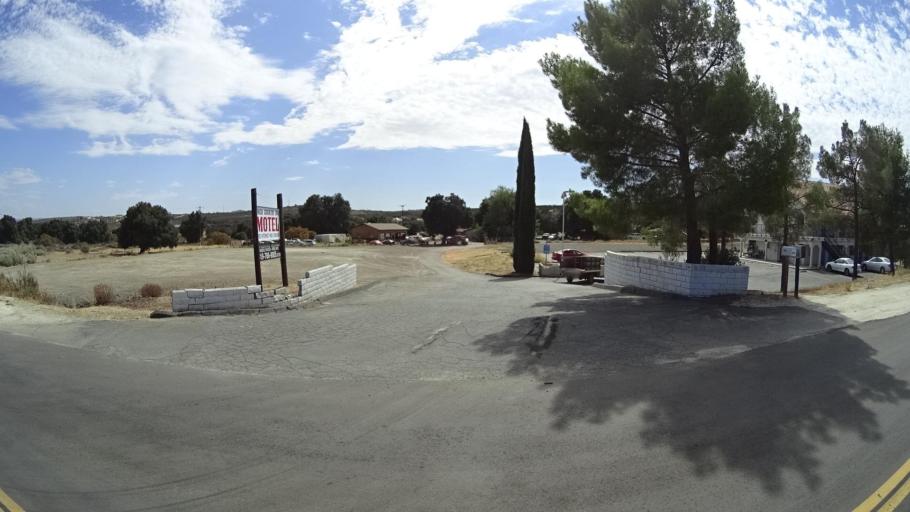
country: US
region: California
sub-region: San Diego County
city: Campo
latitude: 32.6761
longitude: -116.2924
